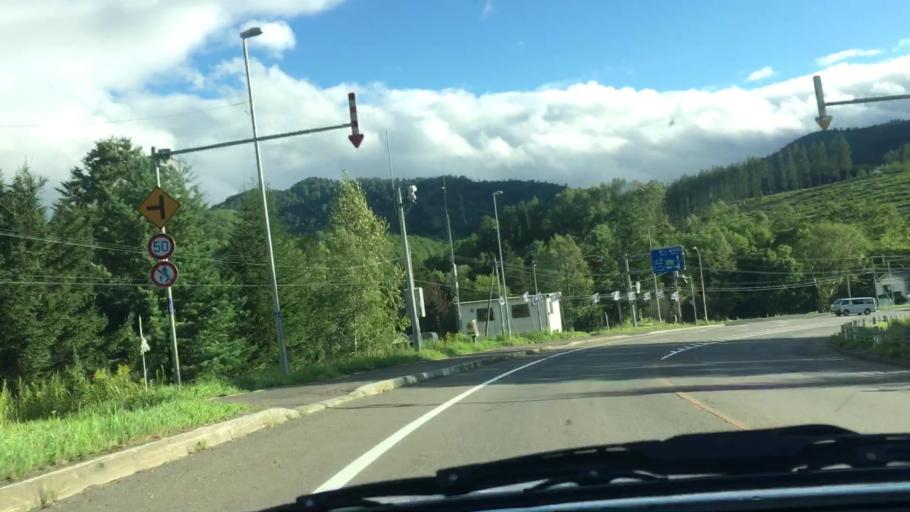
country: JP
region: Hokkaido
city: Shimo-furano
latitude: 43.1251
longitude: 142.6777
